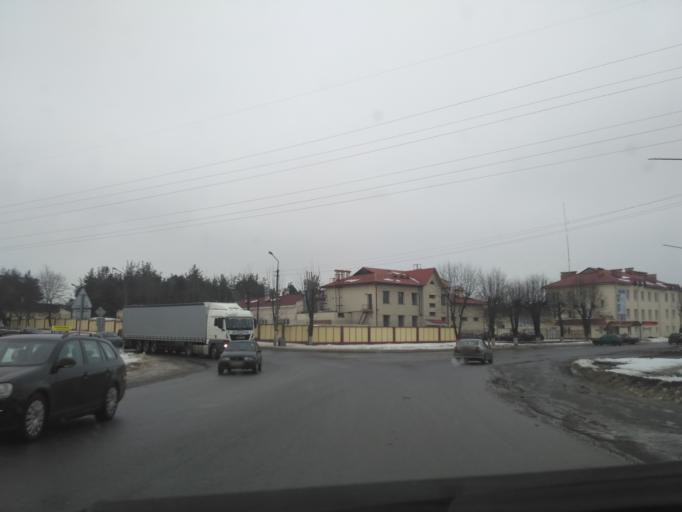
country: BY
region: Minsk
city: Horad Barysaw
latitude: 54.1974
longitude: 28.5145
